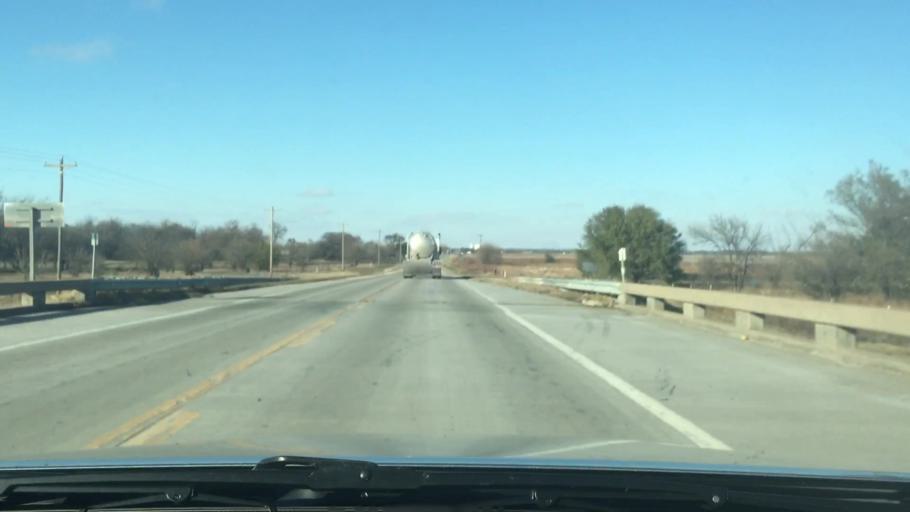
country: US
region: Kansas
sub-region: Rice County
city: Sterling
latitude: 38.1708
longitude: -98.2068
